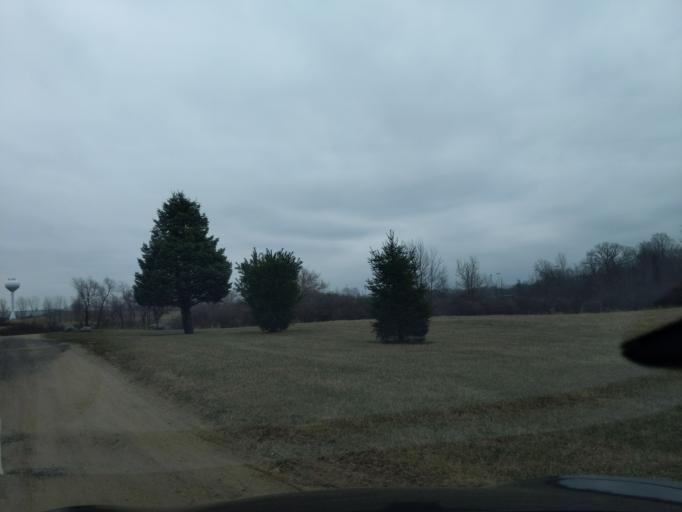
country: US
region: Michigan
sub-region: Eaton County
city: Potterville
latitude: 42.6211
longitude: -84.7572
